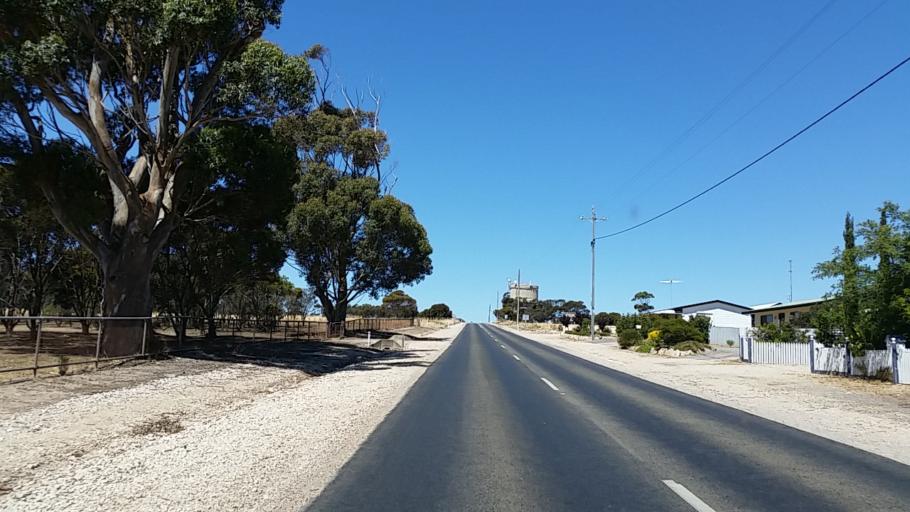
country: AU
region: South Australia
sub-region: Yorke Peninsula
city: Honiton
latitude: -35.0173
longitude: 137.6158
